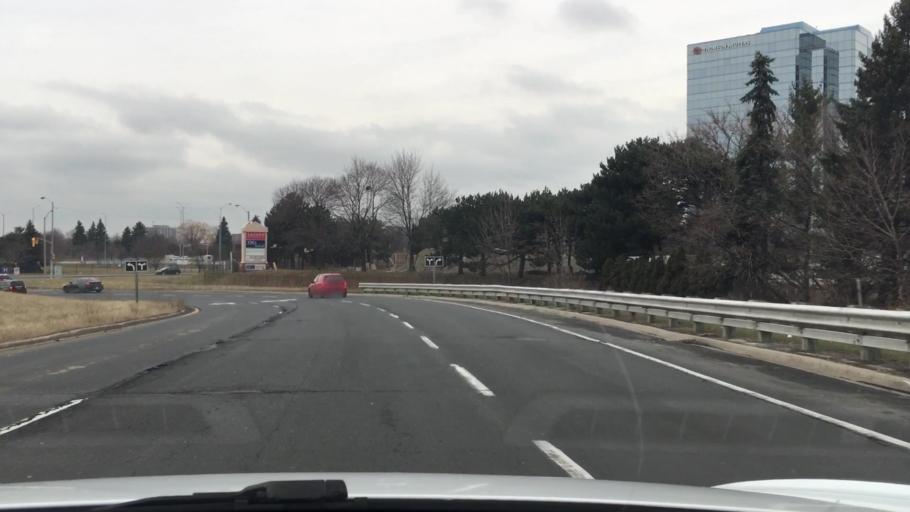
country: CA
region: Ontario
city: Scarborough
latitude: 43.7764
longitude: -79.2835
